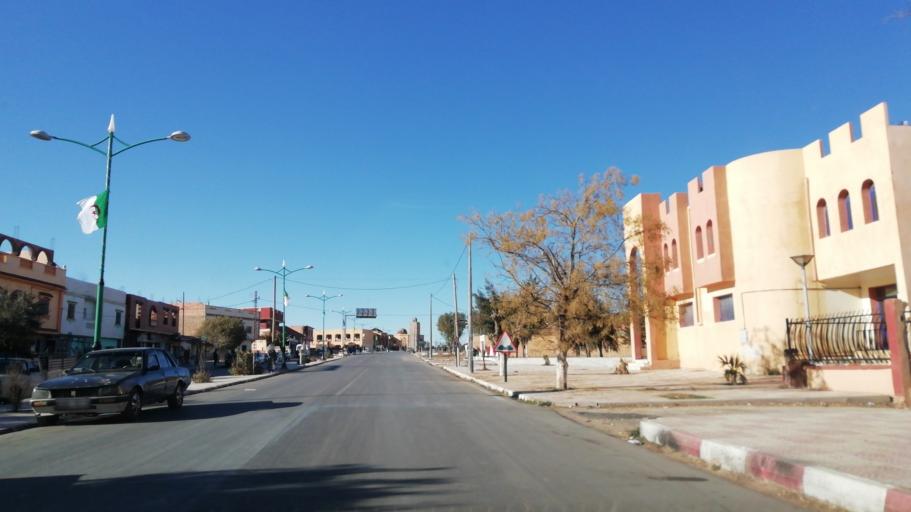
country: DZ
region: Tlemcen
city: Sebdou
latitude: 34.2248
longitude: -1.2538
